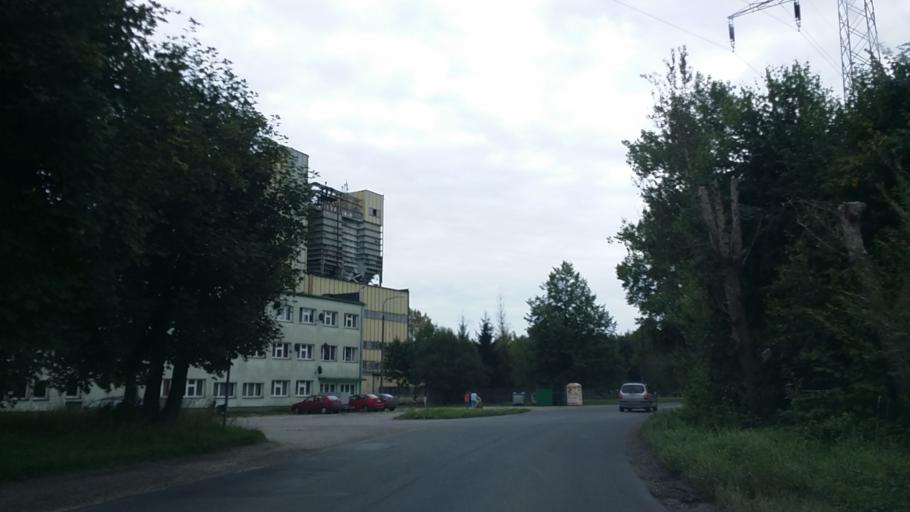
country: PL
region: Lesser Poland Voivodeship
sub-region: Powiat krakowski
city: Skawina
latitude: 49.9810
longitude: 19.8112
